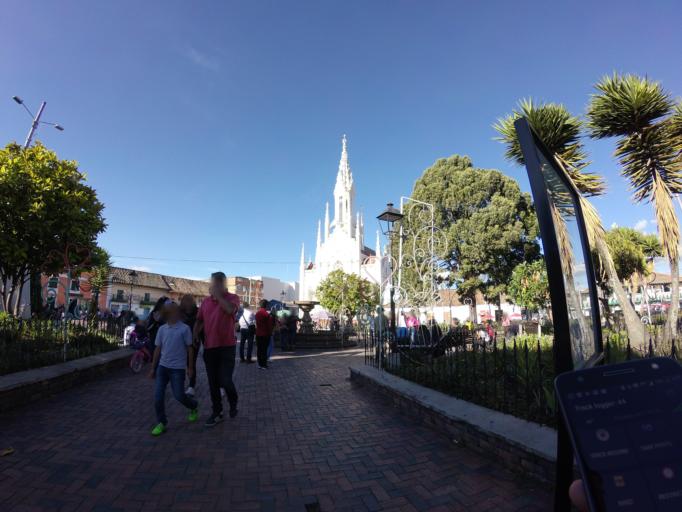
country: CO
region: Cundinamarca
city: Ubate
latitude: 5.3066
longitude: -73.8149
